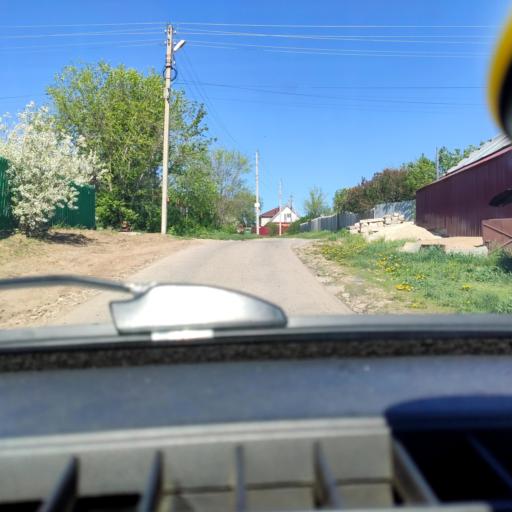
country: RU
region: Samara
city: Zhigulevsk
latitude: 53.5408
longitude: 49.5202
